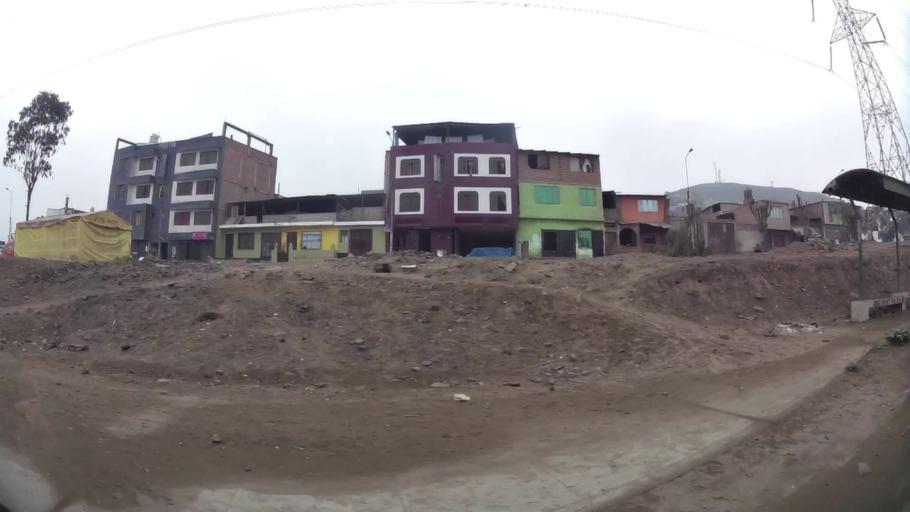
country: PE
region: Lima
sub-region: Lima
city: Surco
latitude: -12.2080
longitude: -76.9267
